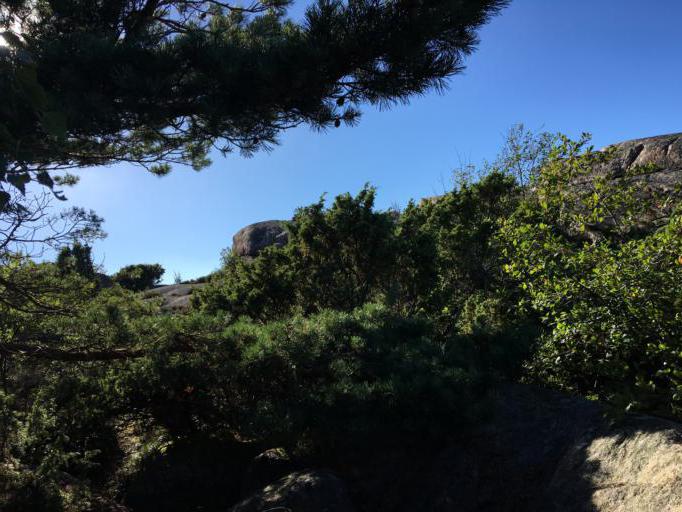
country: SE
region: Vaestra Goetaland
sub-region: Sotenas Kommun
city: Hunnebostrand
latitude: 58.4377
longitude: 11.2504
